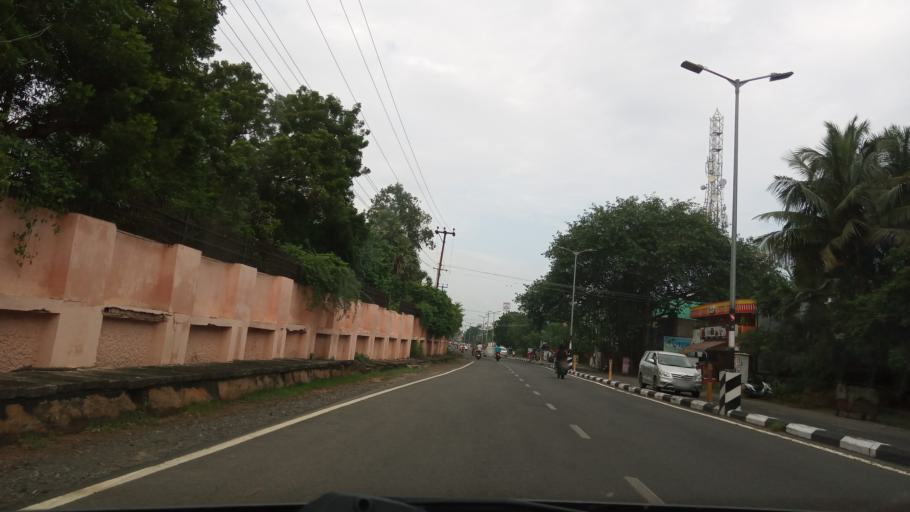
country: IN
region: Tamil Nadu
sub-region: Villupuram
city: Auroville
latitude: 12.0168
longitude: 79.8589
